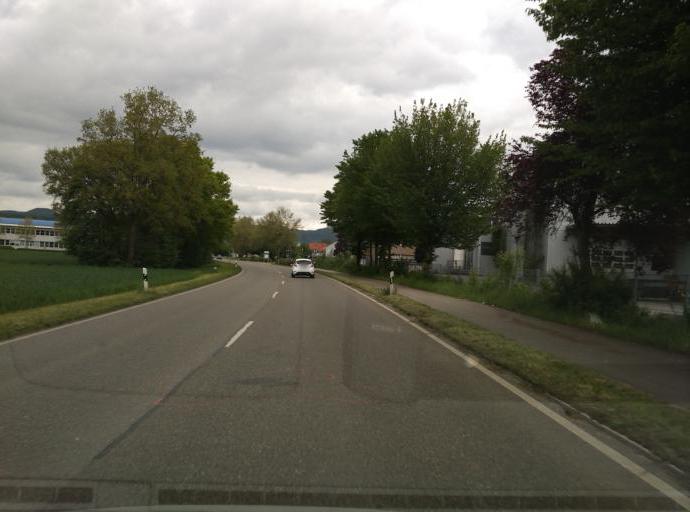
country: DE
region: Baden-Wuerttemberg
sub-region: Regierungsbezirk Stuttgart
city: Frickenhausen
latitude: 48.6008
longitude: 9.3505
